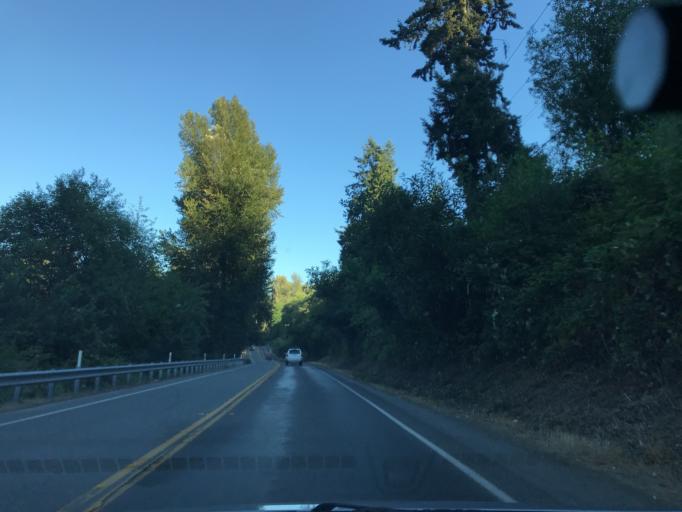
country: US
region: Washington
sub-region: King County
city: Auburn
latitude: 47.2700
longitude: -122.2061
